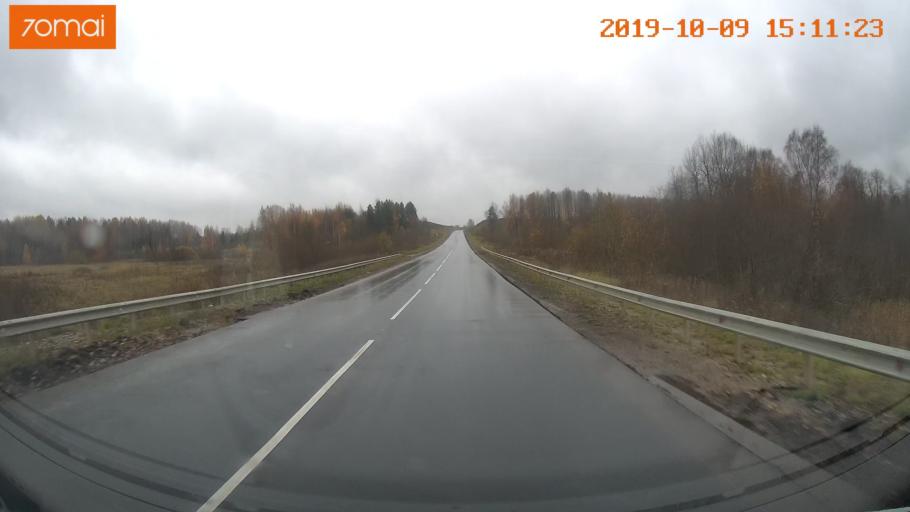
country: RU
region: Kostroma
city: Susanino
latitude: 58.1658
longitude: 41.6303
